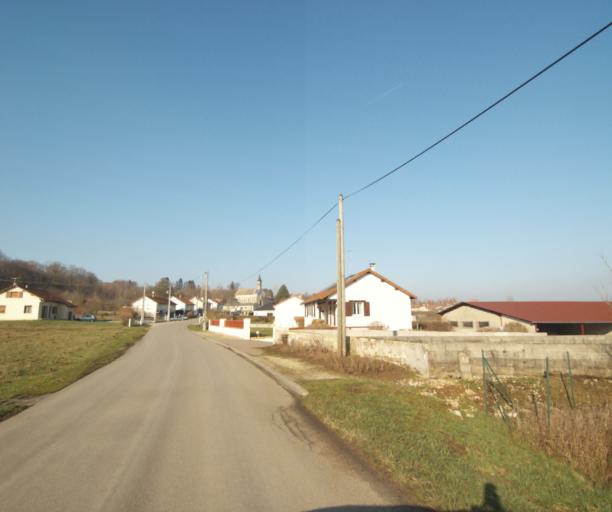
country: FR
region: Champagne-Ardenne
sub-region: Departement de la Haute-Marne
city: Wassy
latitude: 48.5117
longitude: 4.9187
